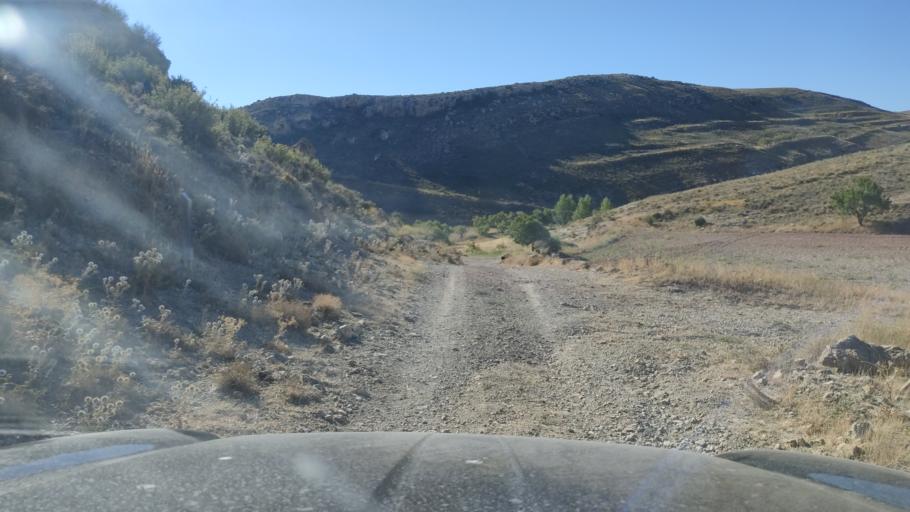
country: ES
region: Aragon
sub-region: Provincia de Teruel
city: Monforte de Moyuela
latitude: 41.0475
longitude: -1.0142
